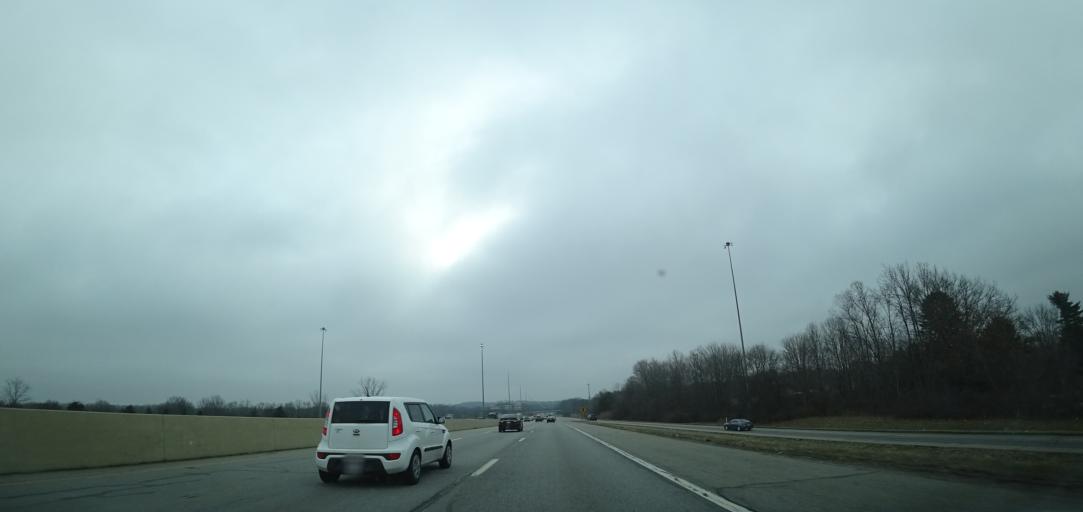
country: US
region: Ohio
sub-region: Summit County
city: Fairlawn
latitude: 41.1192
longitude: -81.6379
